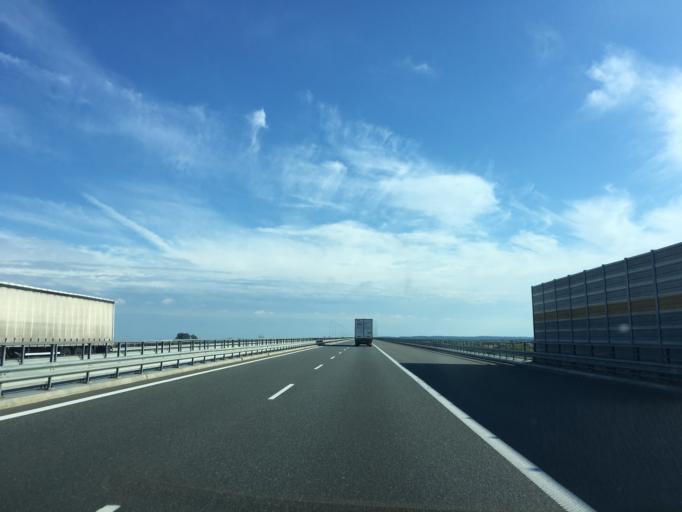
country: PL
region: Kujawsko-Pomorskie
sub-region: Grudziadz
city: Grudziadz
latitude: 53.4474
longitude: 18.6728
